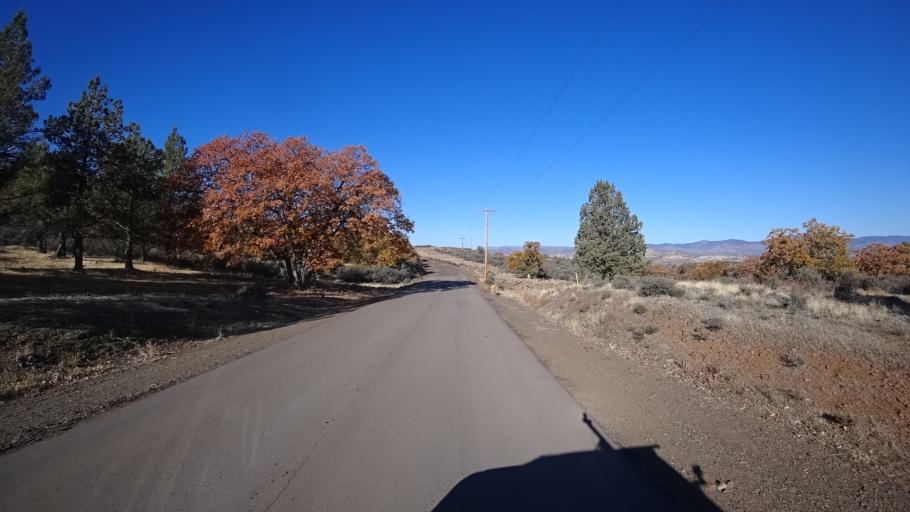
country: US
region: California
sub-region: Siskiyou County
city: Montague
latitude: 41.9031
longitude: -122.4312
